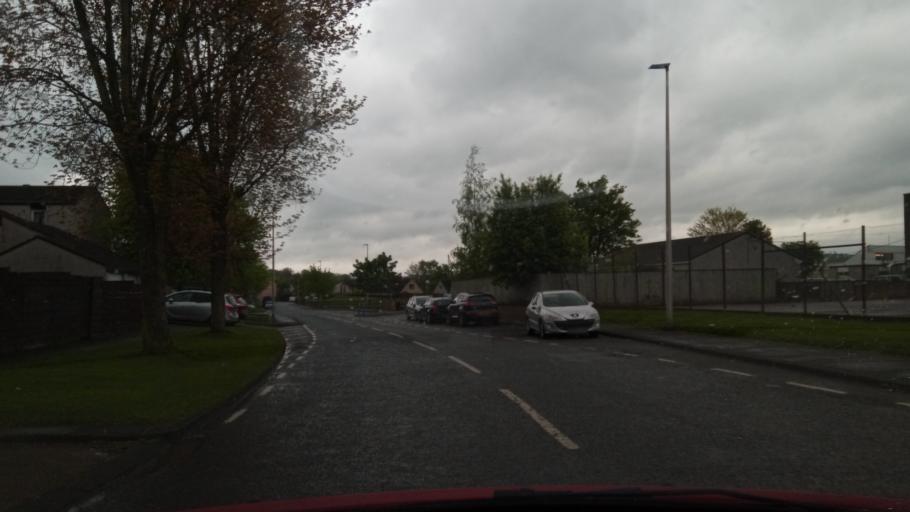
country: GB
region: Scotland
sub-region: The Scottish Borders
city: Jedburgh
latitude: 55.4749
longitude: -2.5457
